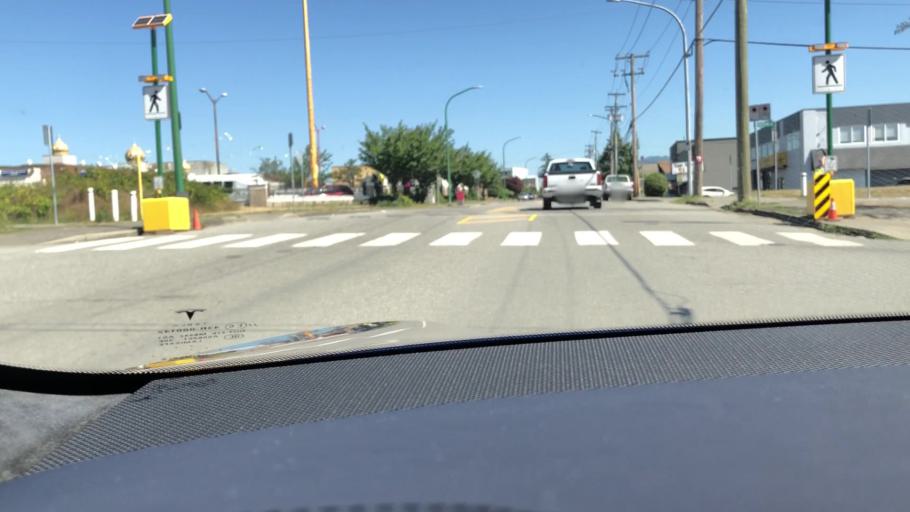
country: CA
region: British Columbia
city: Burnaby
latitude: 49.2171
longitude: -122.9721
